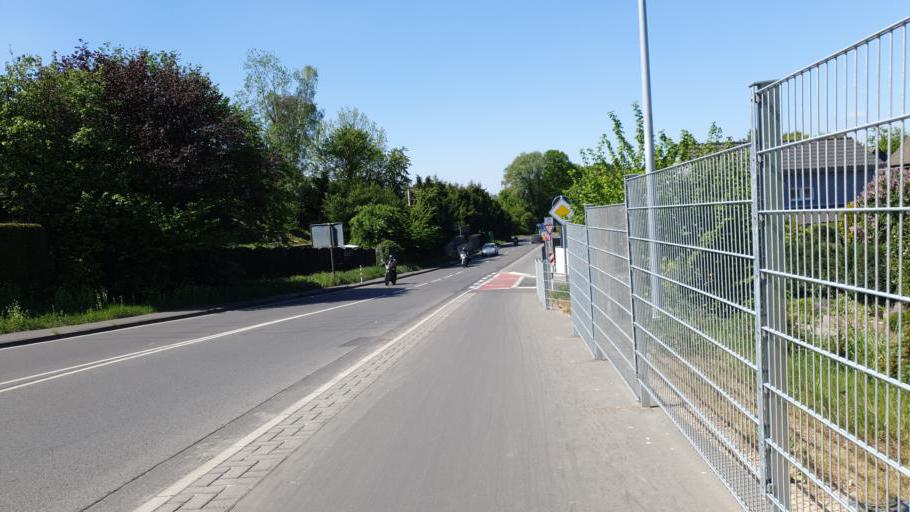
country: DE
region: North Rhine-Westphalia
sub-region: Regierungsbezirk Koln
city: Odenthal
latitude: 51.0224
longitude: 7.0844
